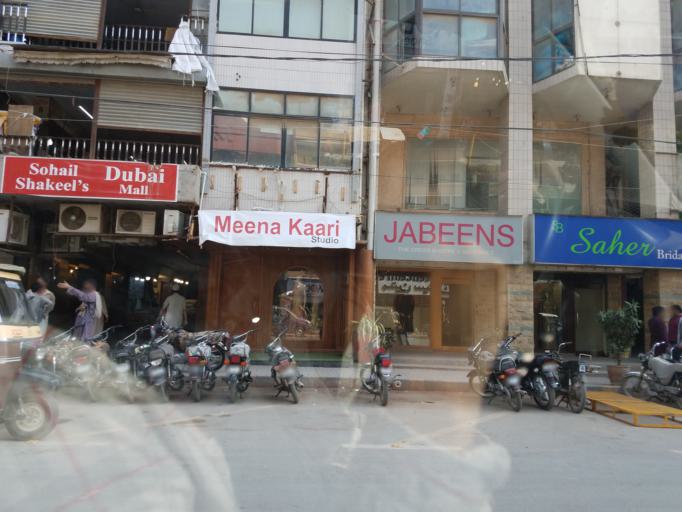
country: PK
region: Sindh
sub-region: Karachi District
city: Karachi
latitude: 24.8748
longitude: 67.0619
